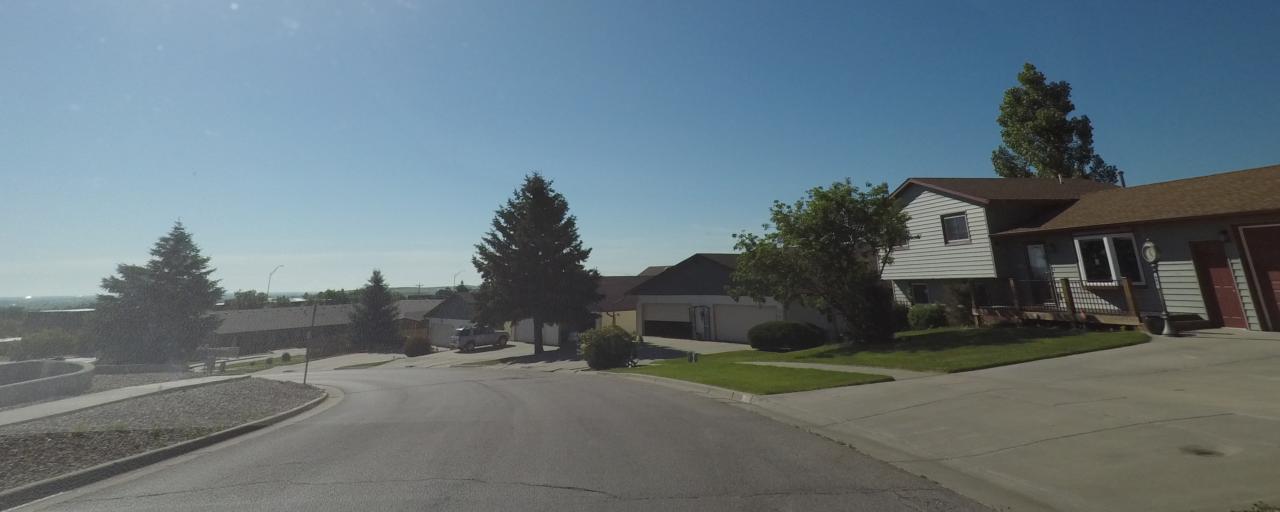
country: US
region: South Dakota
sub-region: Pennington County
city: Rapid City
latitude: 44.0501
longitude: -103.2258
